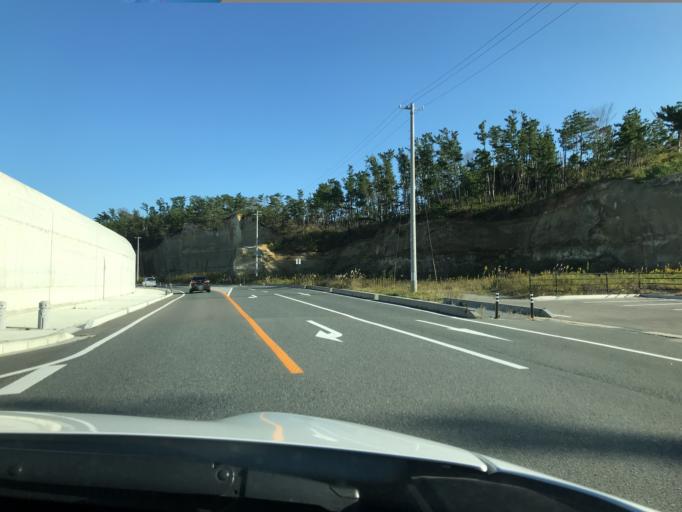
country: JP
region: Miyagi
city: Marumori
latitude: 37.8243
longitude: 140.9802
